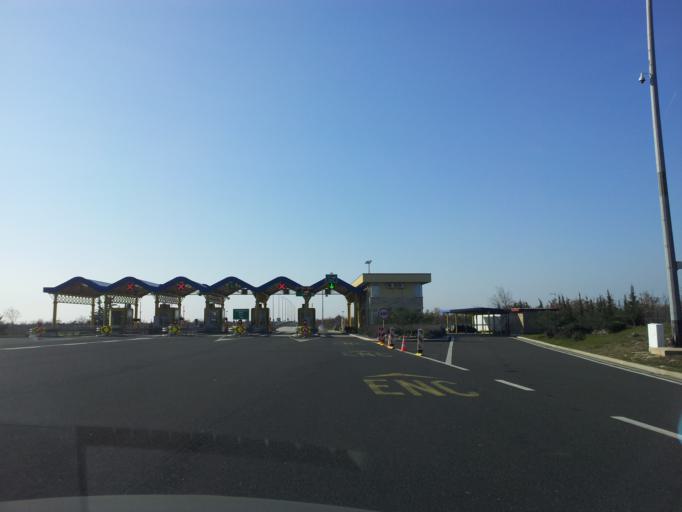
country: HR
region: Zadarska
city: Galovac
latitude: 44.1145
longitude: 15.4380
